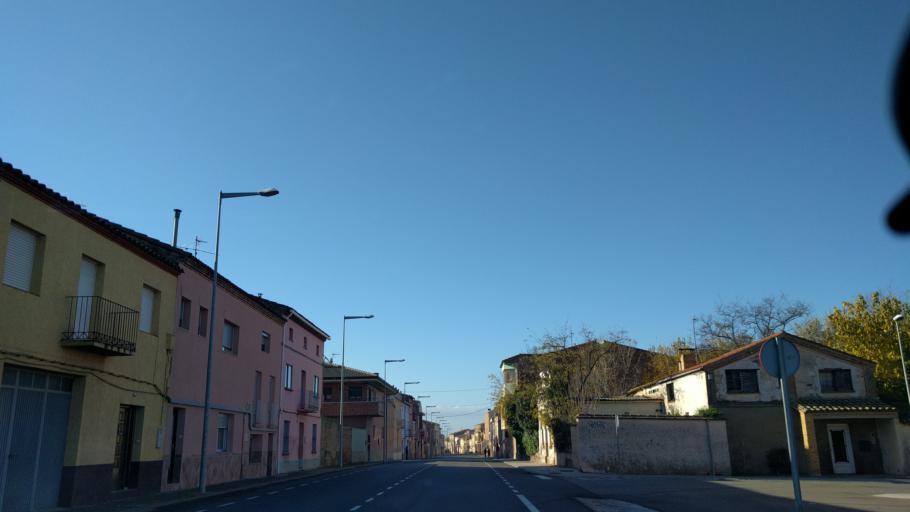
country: ES
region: Catalonia
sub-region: Provincia de Lleida
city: Corbins
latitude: 41.6897
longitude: 0.7296
